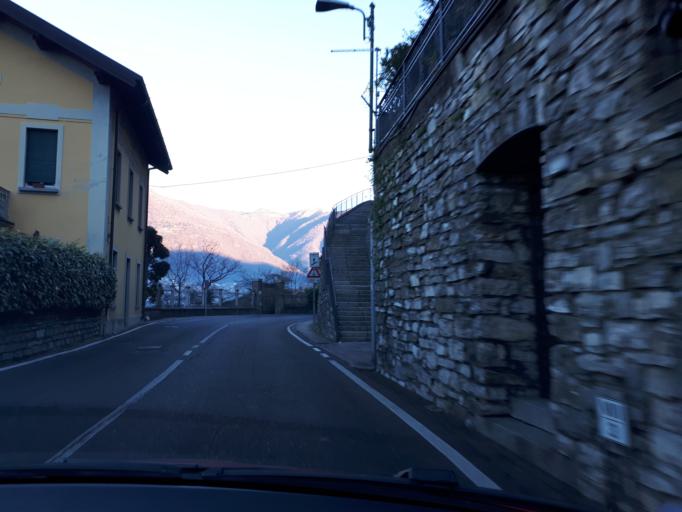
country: IT
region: Lombardy
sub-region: Provincia di Como
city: Blevio
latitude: 45.8390
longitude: 9.1033
